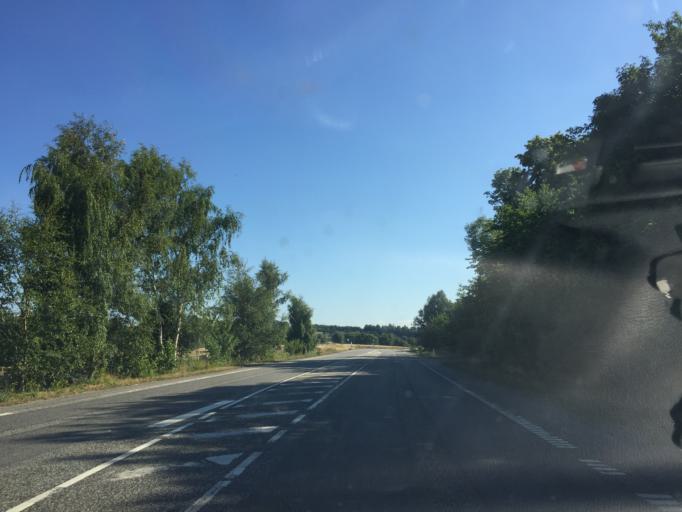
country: DK
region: Capital Region
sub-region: Egedal Kommune
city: Smorumnedre
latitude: 55.7622
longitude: 12.2938
